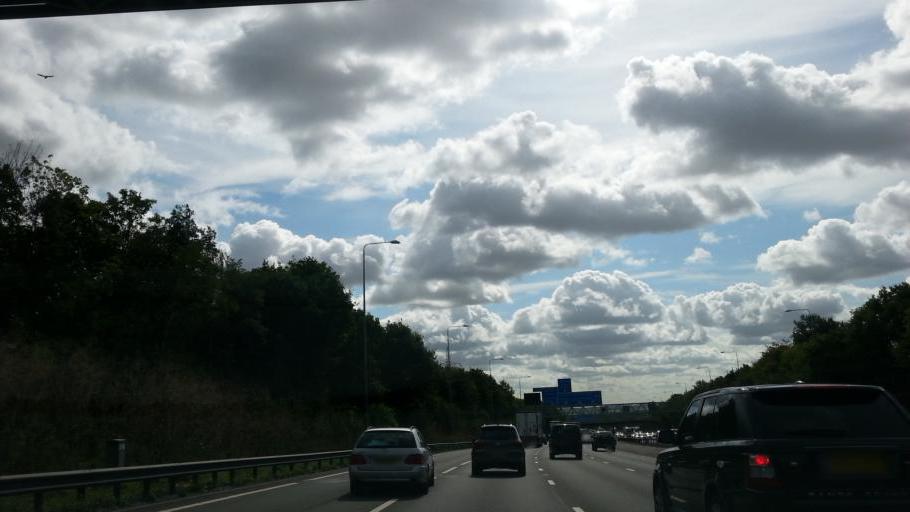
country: GB
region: England
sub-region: Essex
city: Theydon Bois
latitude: 51.6881
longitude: 0.0999
